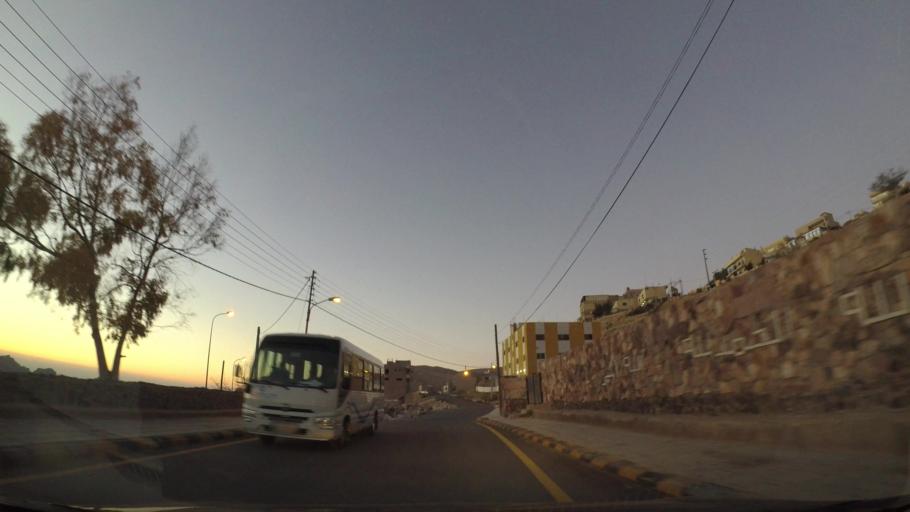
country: JO
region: Ma'an
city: Petra
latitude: 30.3201
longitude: 35.4825
